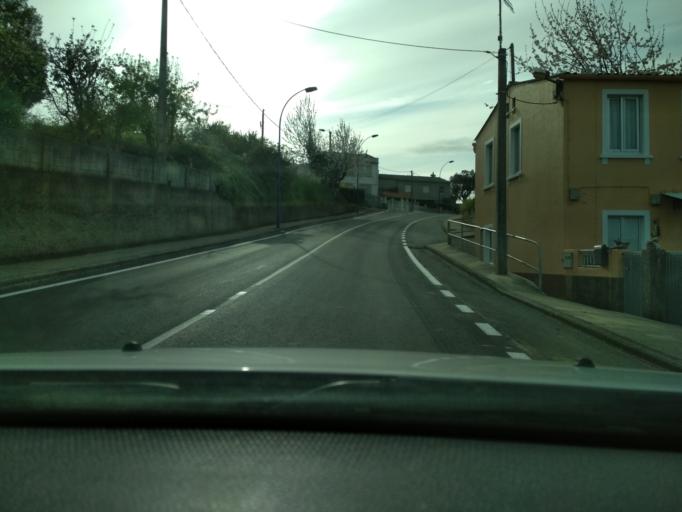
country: ES
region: Galicia
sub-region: Provincia da Coruna
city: Culleredo
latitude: 43.2870
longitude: -8.3873
